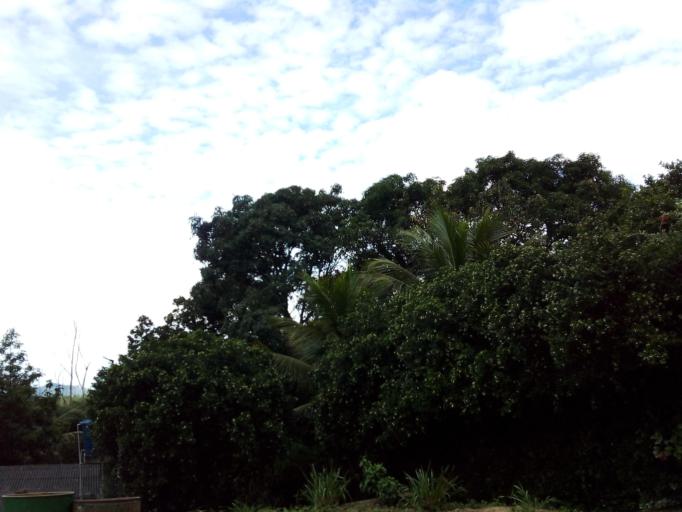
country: BR
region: Espirito Santo
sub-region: Joao Neiva
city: Joao Neiva
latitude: -19.7779
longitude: -40.3712
